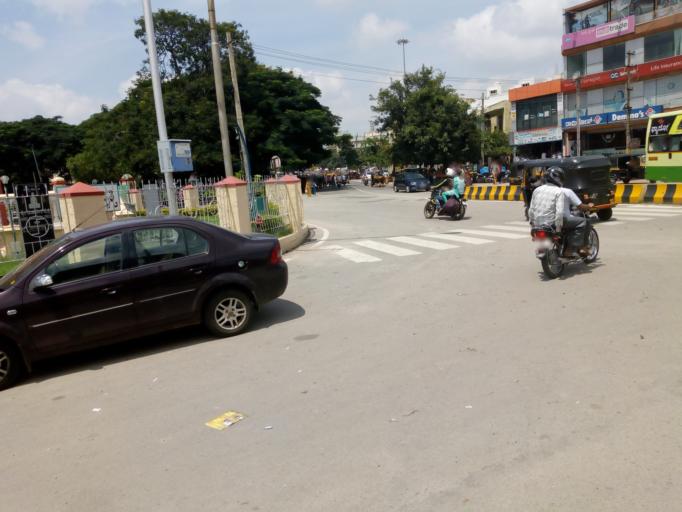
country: IN
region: Karnataka
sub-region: Mysore
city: Mysore
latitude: 12.3098
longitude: 76.6560
